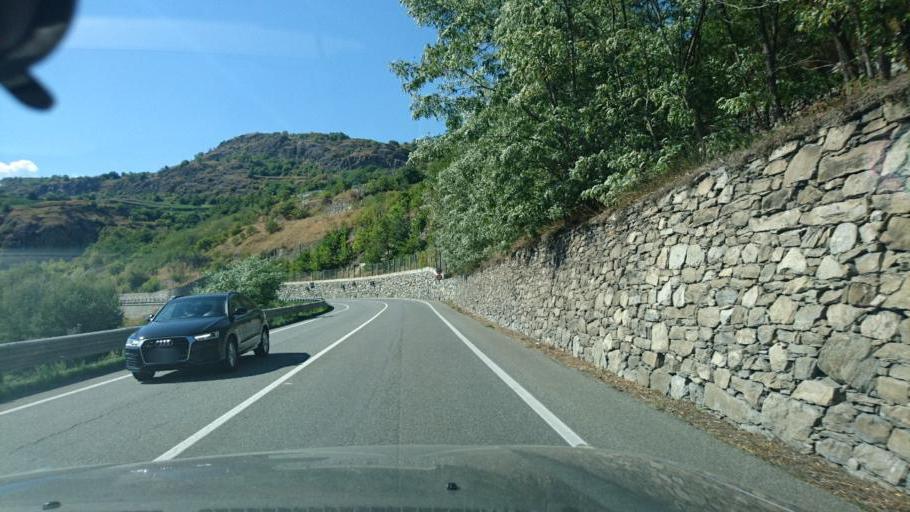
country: IT
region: Aosta Valley
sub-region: Valle d'Aosta
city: Saint Maurice
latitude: 45.7123
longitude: 7.2518
